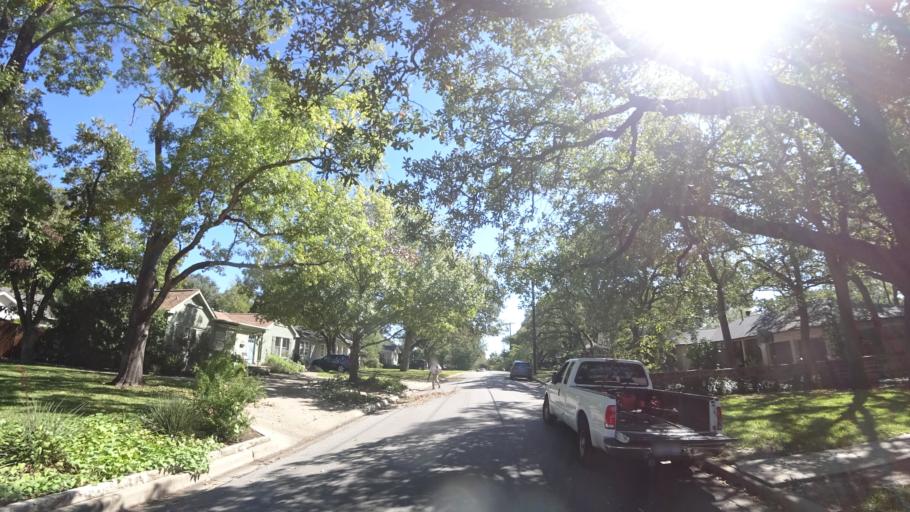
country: US
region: Texas
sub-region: Travis County
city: Rollingwood
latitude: 30.2975
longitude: -97.7664
